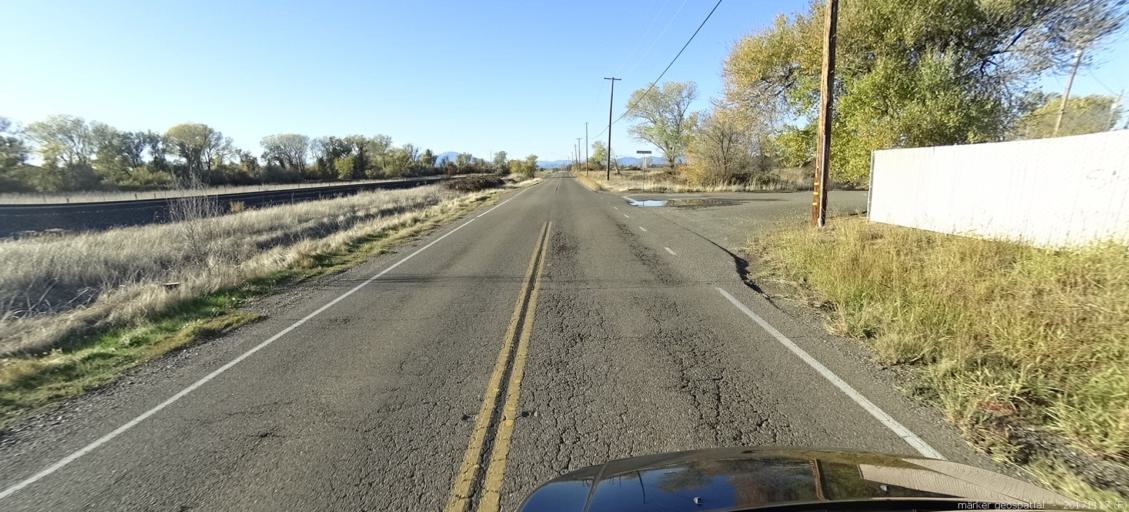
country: US
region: California
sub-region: Shasta County
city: Cottonwood
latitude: 40.4223
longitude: -122.2593
